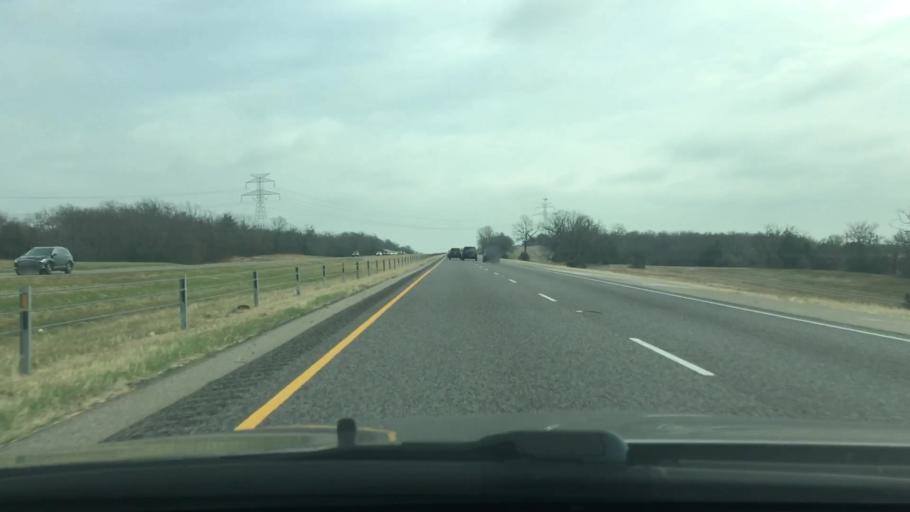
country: US
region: Texas
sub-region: Leon County
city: Buffalo
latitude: 31.5389
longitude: -96.1220
